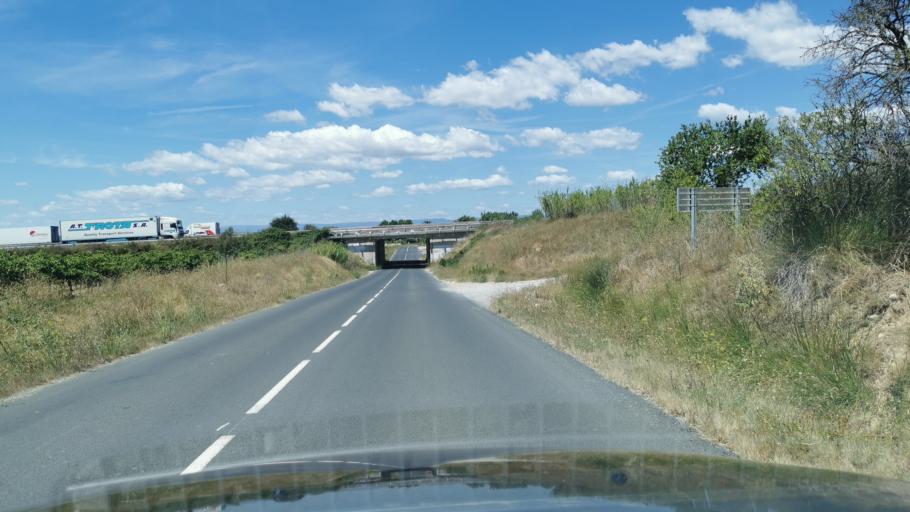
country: FR
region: Languedoc-Roussillon
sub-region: Departement de l'Aude
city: Vinassan
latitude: 43.1946
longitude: 3.0751
